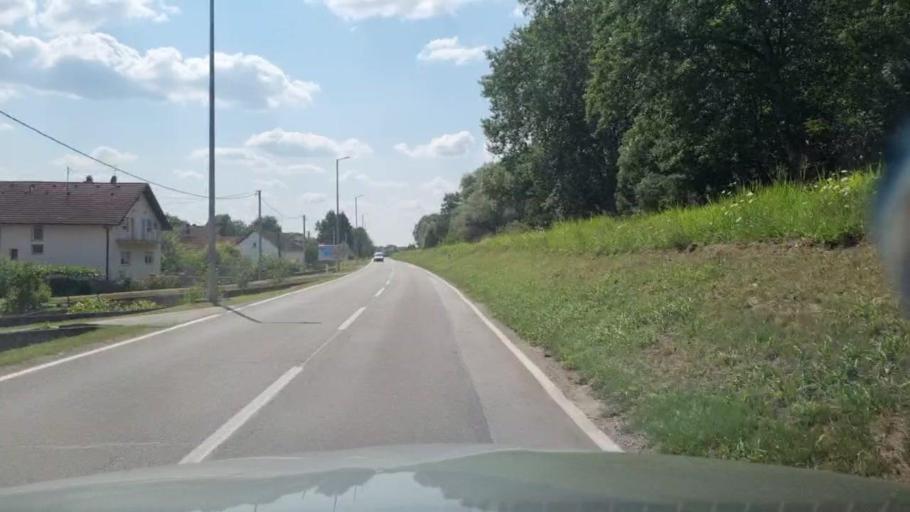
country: HR
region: Vukovarsko-Srijemska
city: Stitar
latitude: 45.0638
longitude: 18.5933
